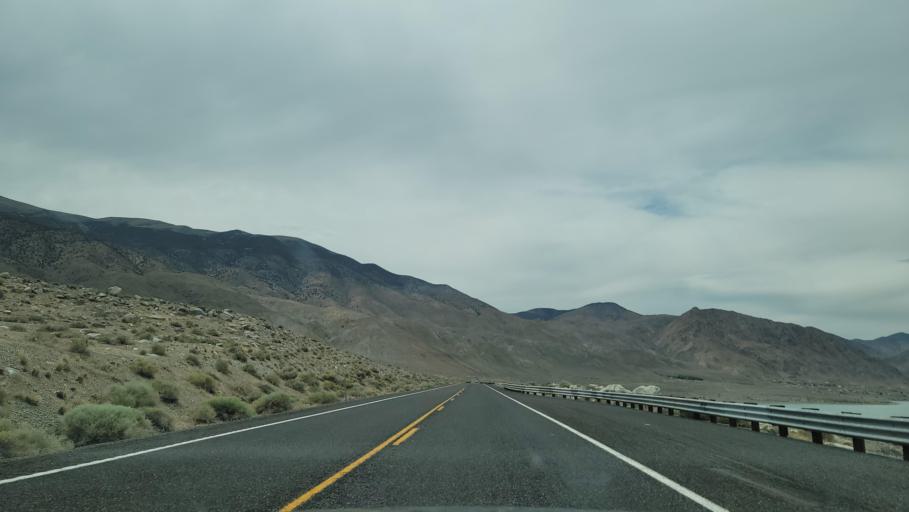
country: US
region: Nevada
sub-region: Mineral County
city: Hawthorne
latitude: 38.6134
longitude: -118.7221
